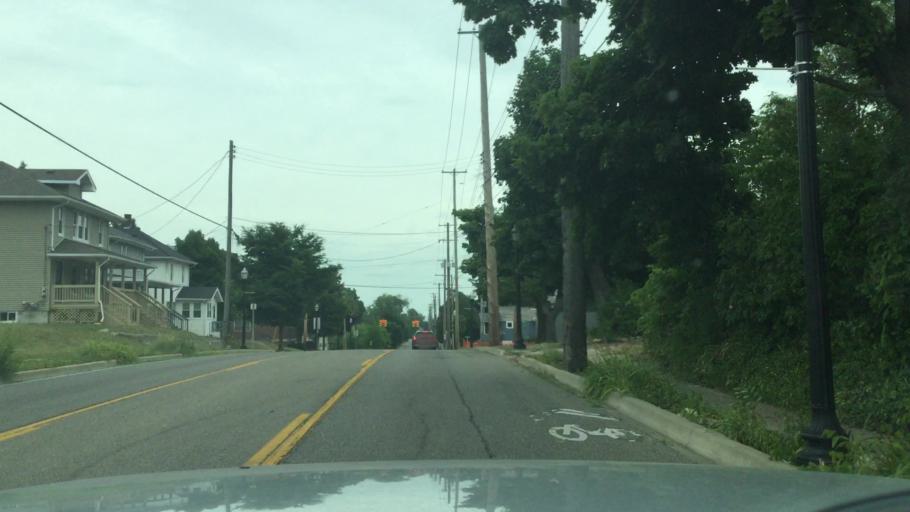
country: US
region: Michigan
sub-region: Genesee County
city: Flint
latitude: 43.0156
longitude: -83.7075
